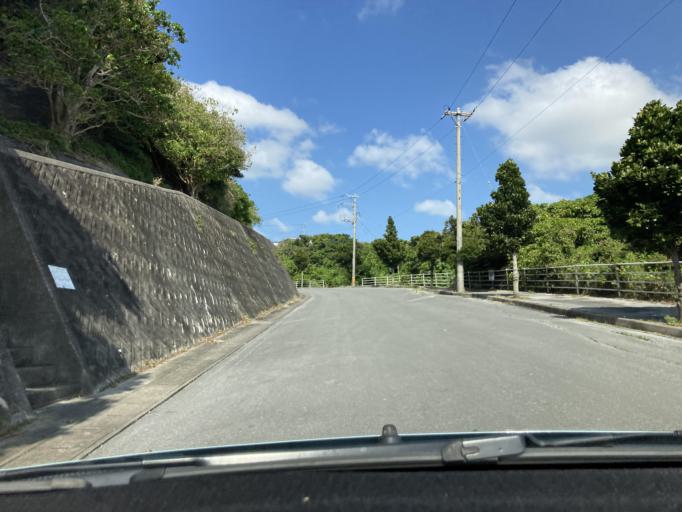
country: JP
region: Okinawa
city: Itoman
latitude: 26.1219
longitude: 127.7511
